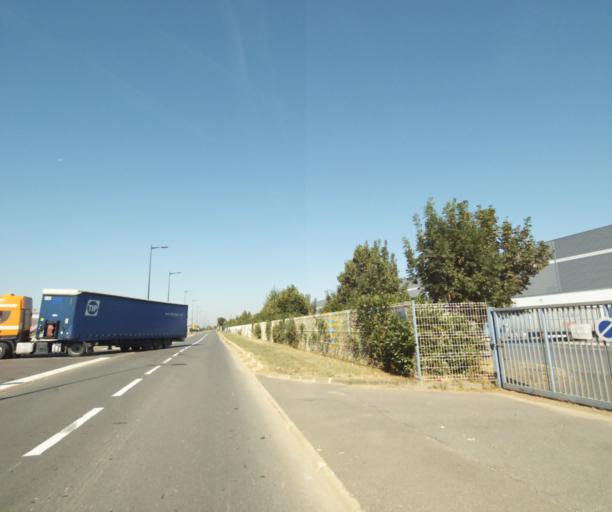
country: FR
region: Ile-de-France
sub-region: Departement de Seine-et-Marne
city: Moissy-Cramayel
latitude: 48.6115
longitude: 2.5930
